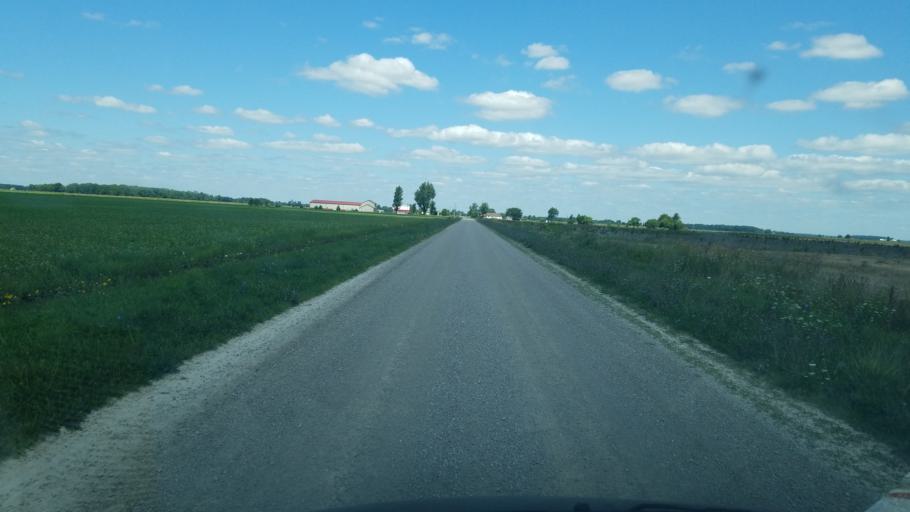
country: US
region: Ohio
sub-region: Fulton County
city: Delta
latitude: 41.7226
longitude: -84.0182
